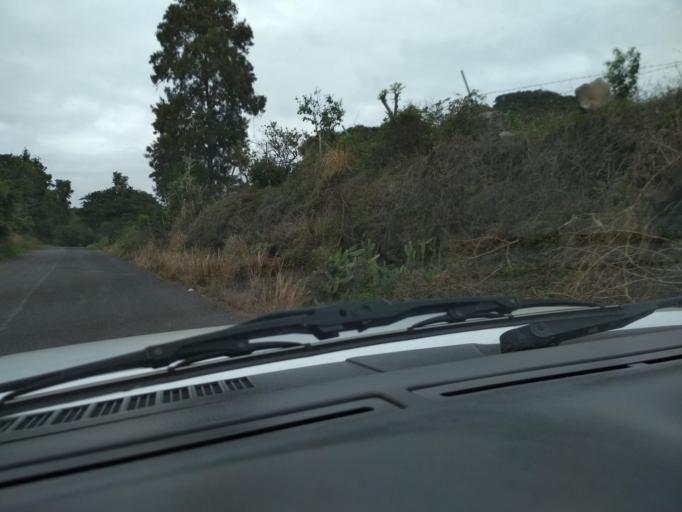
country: MX
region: Veracruz
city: Alto Lucero
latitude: 19.5941
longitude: -96.7925
